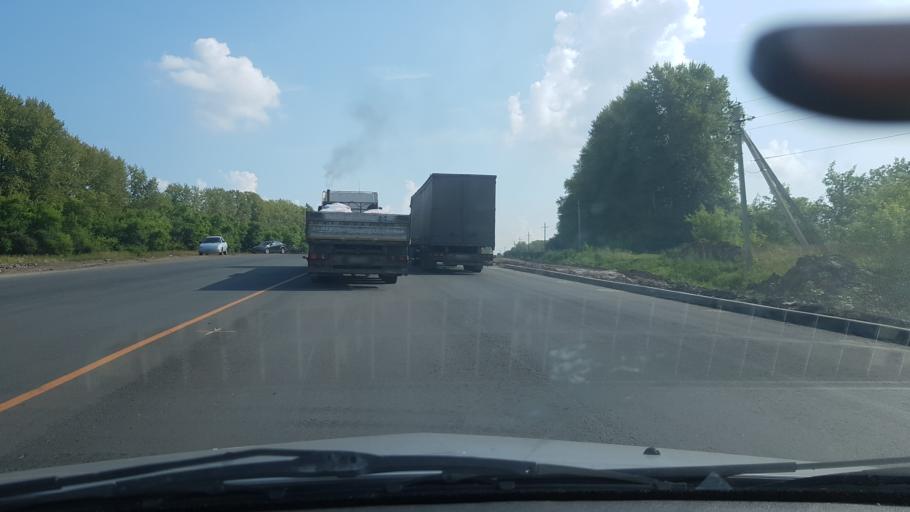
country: RU
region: Chuvashia
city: Tsivil'sk
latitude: 55.7302
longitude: 47.4481
